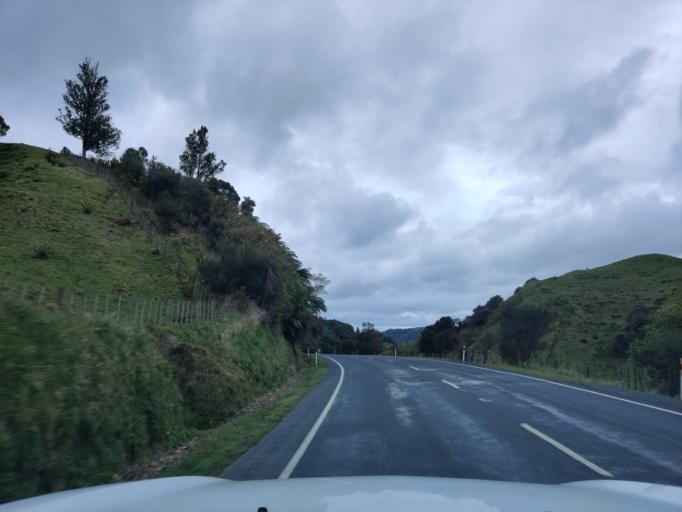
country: NZ
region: Waikato
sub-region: Otorohanga District
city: Otorohanga
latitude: -38.5107
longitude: 175.2069
